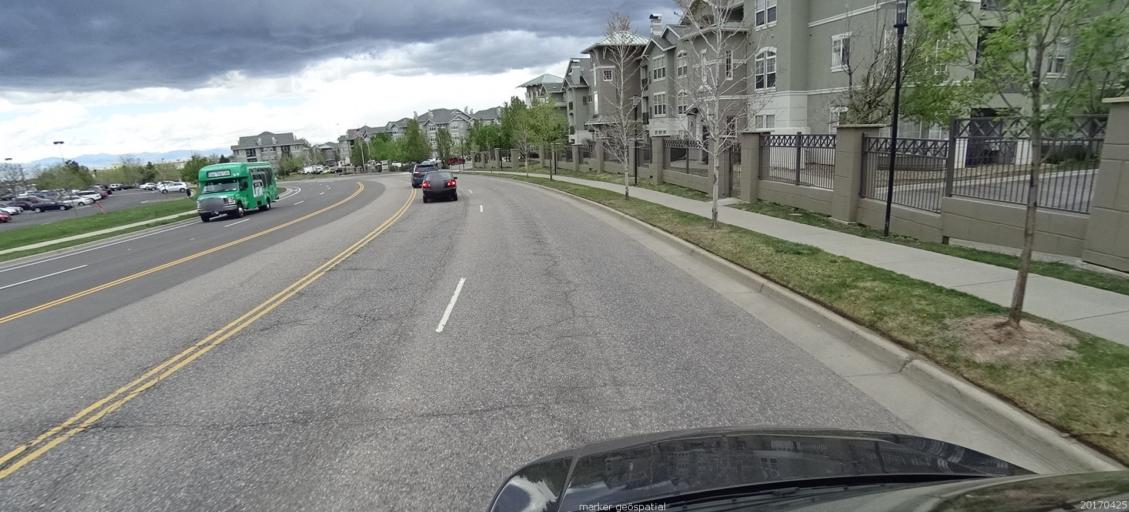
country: US
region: Colorado
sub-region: Douglas County
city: Meridian
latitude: 39.5512
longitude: -104.8719
